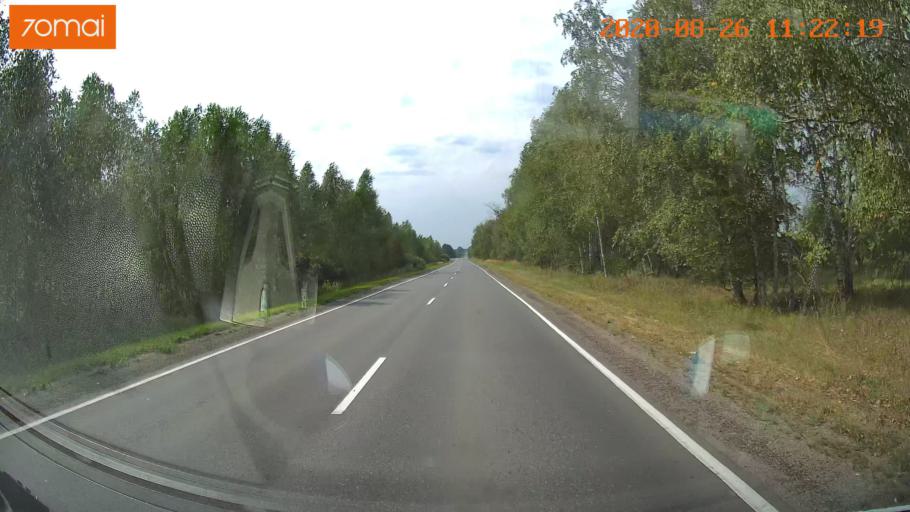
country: RU
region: Rjazan
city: Shilovo
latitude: 54.3654
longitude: 41.0292
